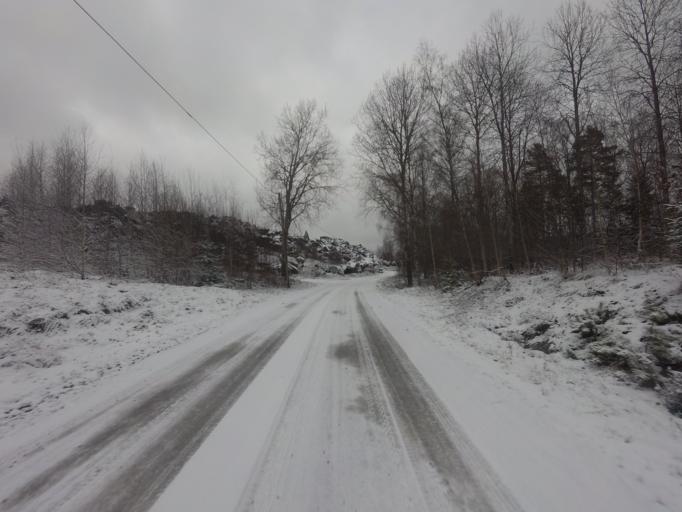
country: SE
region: Skane
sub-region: Osby Kommun
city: Lonsboda
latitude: 56.3972
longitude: 14.2505
